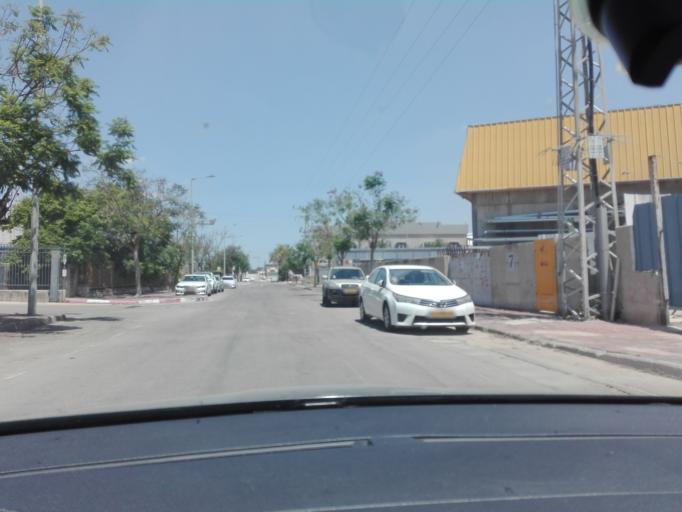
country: IL
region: Southern District
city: Qiryat Gat
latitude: 31.5929
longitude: 34.7806
